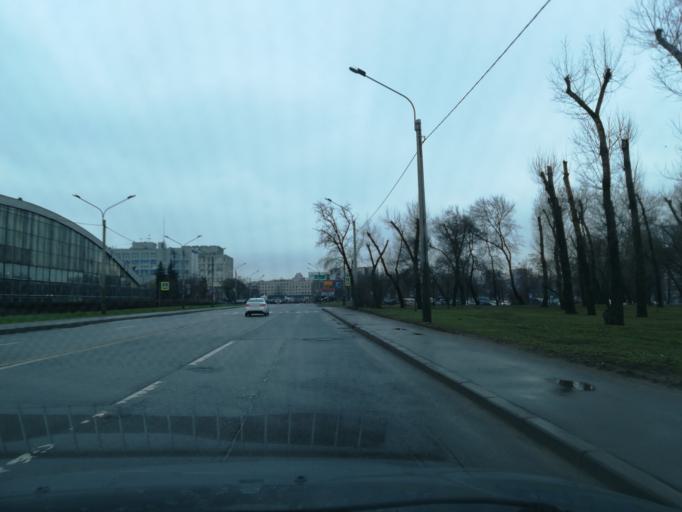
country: RU
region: St.-Petersburg
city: Avtovo
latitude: 59.8609
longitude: 30.2606
